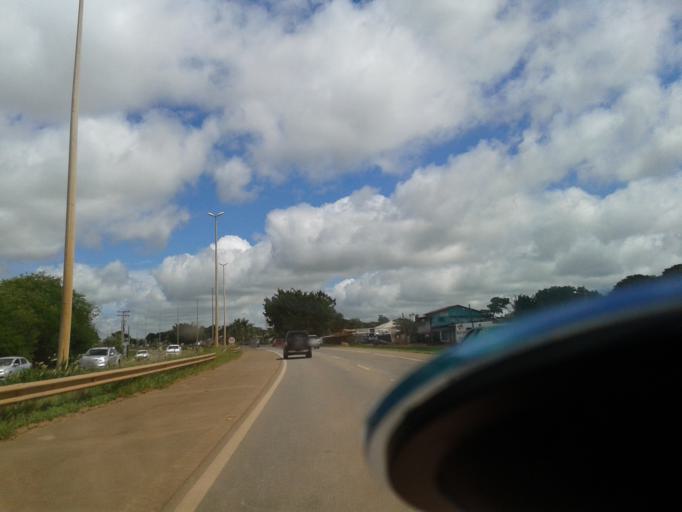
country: BR
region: Goias
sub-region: Goianira
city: Goianira
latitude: -16.5416
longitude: -49.4033
